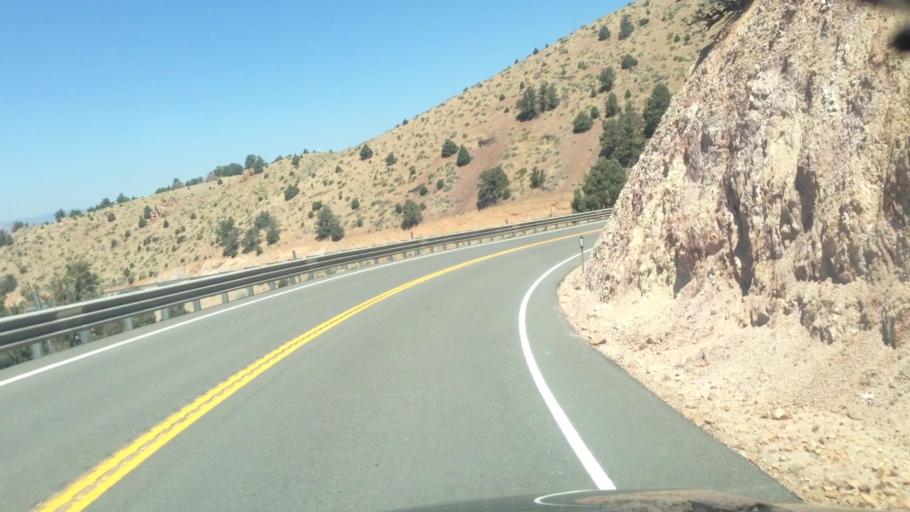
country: US
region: Nevada
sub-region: Storey County
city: Virginia City
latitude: 39.3813
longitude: -119.6964
